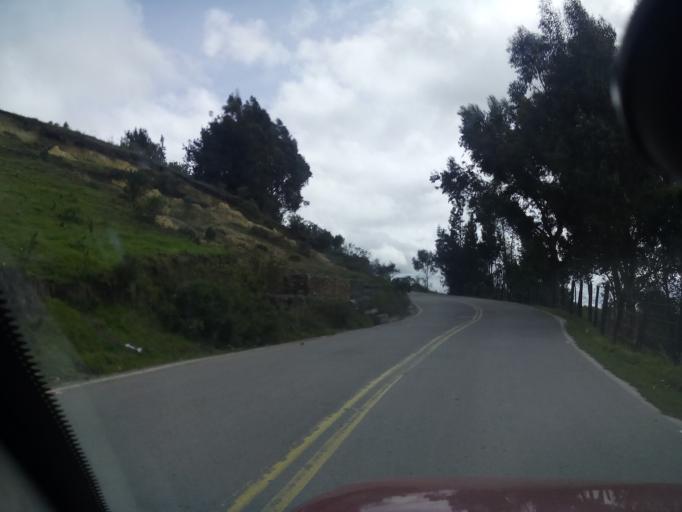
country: CO
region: Boyaca
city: Combita
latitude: 5.6342
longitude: -73.3405
